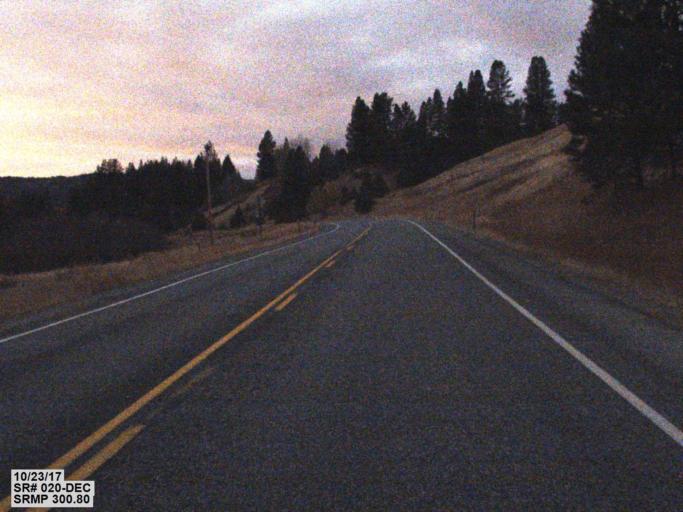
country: US
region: Washington
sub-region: Ferry County
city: Republic
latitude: 48.6493
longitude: -118.7637
